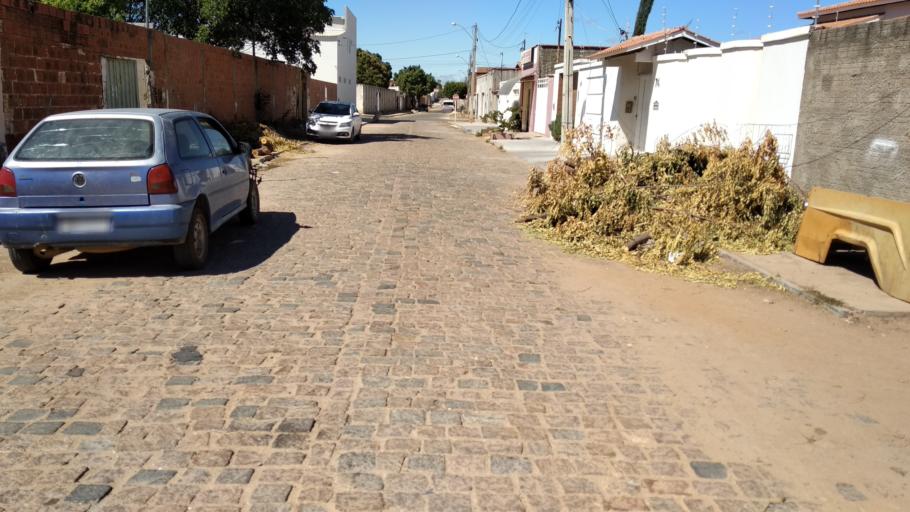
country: BR
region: Bahia
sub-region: Guanambi
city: Guanambi
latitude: -14.2331
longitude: -42.7771
